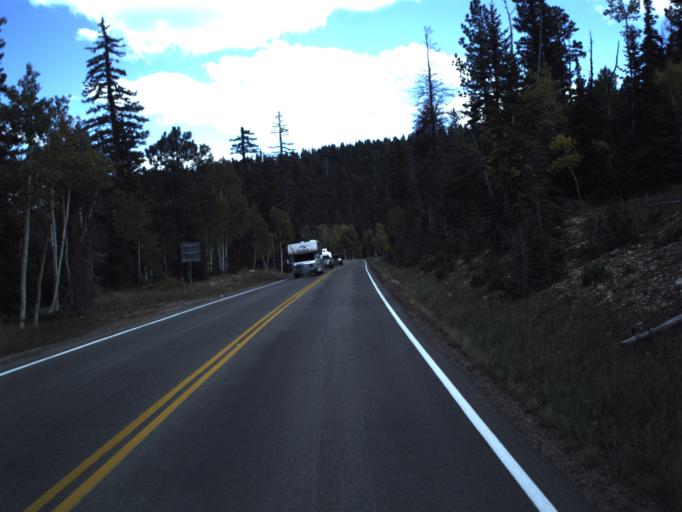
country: US
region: Utah
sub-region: Iron County
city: Parowan
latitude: 37.5147
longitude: -112.6922
